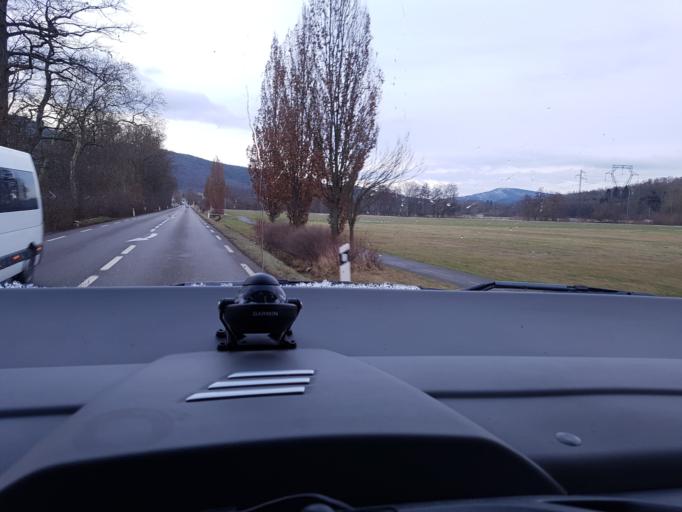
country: FR
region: Alsace
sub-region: Departement du Bas-Rhin
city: Ville
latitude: 48.3232
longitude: 7.3410
